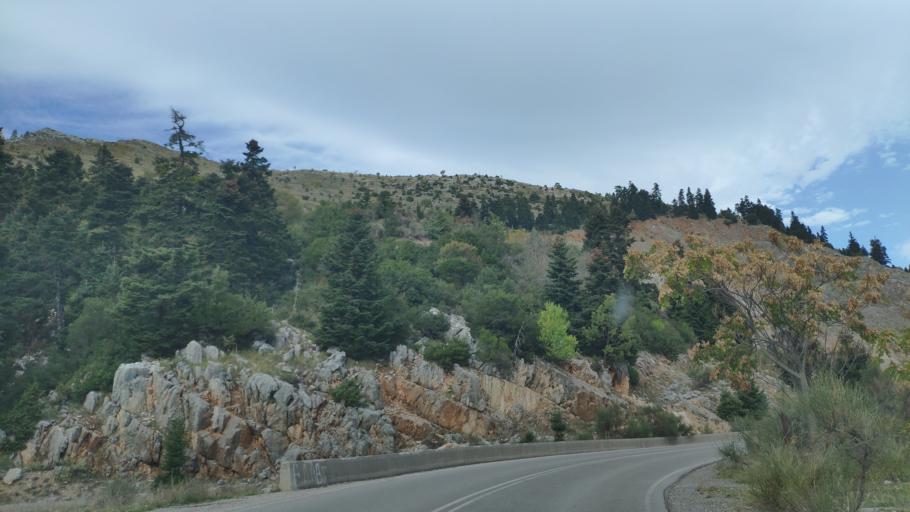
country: GR
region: Central Greece
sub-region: Nomos Fokidos
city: Amfissa
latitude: 38.6519
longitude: 22.3830
